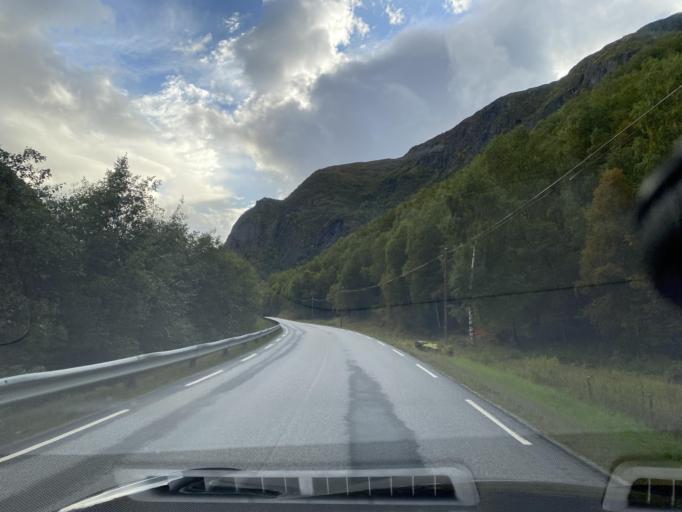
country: NO
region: Oppland
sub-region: Lom
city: Fossbergom
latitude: 61.7860
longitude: 8.4450
